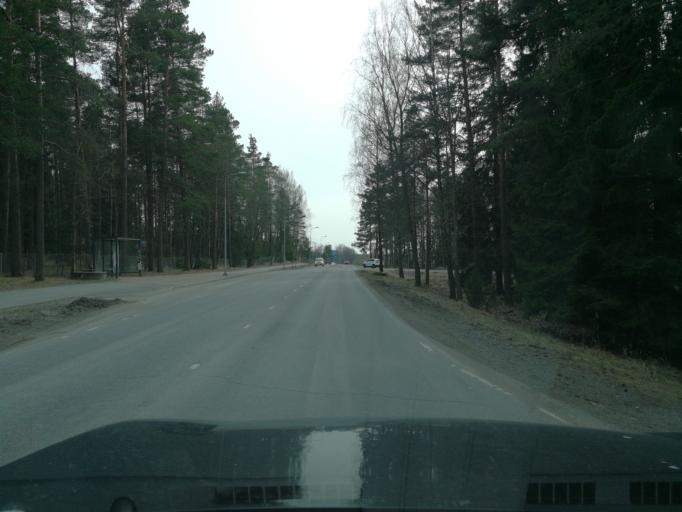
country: FI
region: Uusimaa
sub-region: Helsinki
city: Lohja
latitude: 60.1854
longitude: 23.9950
